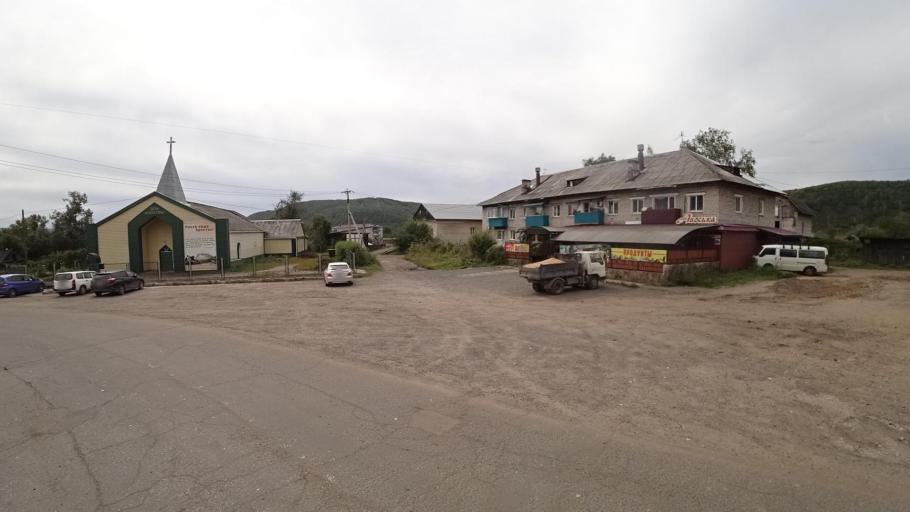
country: RU
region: Jewish Autonomous Oblast
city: Khingansk
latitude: 49.0160
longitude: 131.0546
